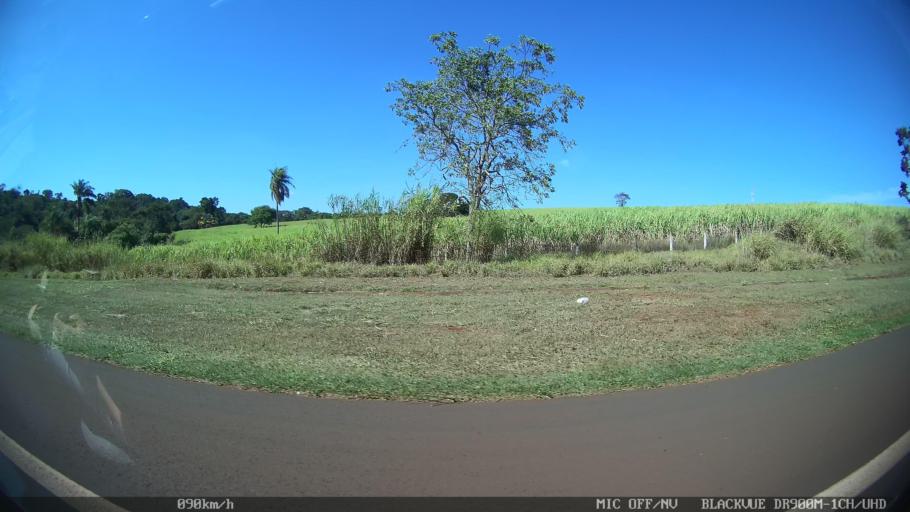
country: BR
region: Sao Paulo
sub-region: Franca
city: Franca
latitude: -20.6361
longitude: -47.4709
